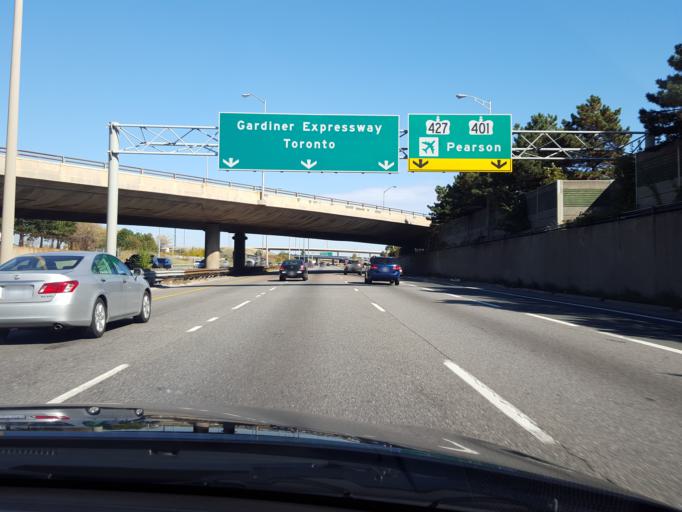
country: CA
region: Ontario
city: Etobicoke
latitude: 43.6089
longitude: -79.5552
